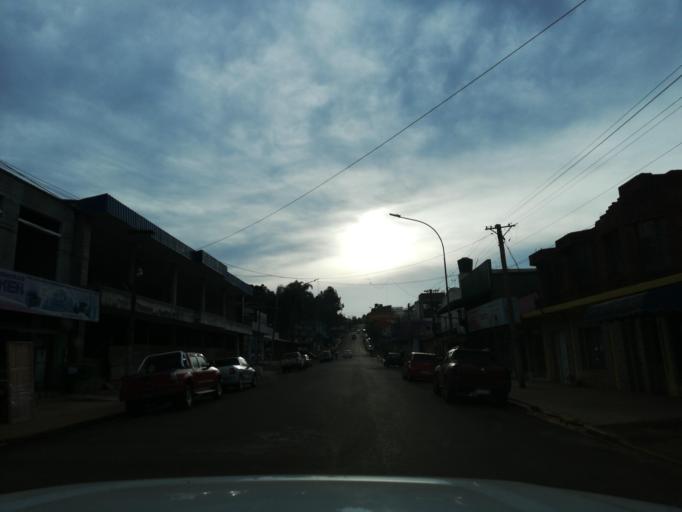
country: AR
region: Misiones
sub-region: Departamento de San Pedro
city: San Pedro
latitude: -26.6236
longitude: -54.1116
